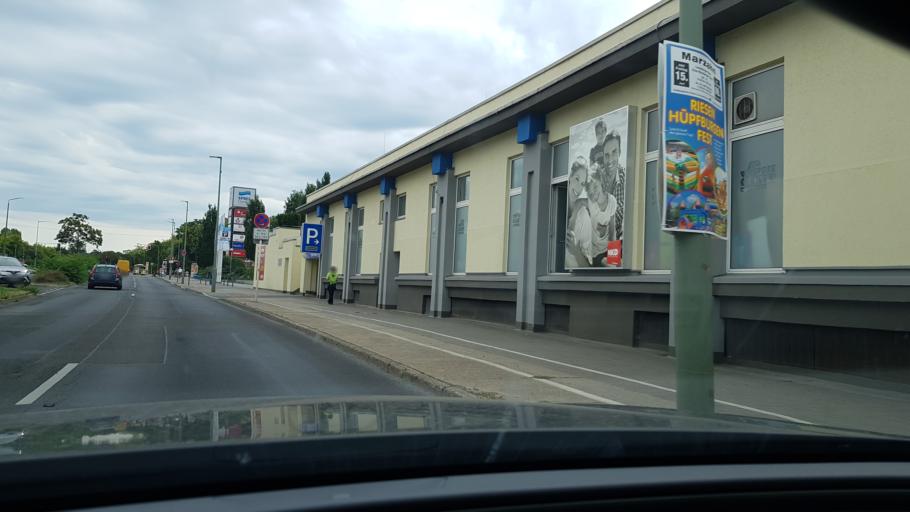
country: DE
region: Berlin
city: Kaulsdorf
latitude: 52.5222
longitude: 13.5873
